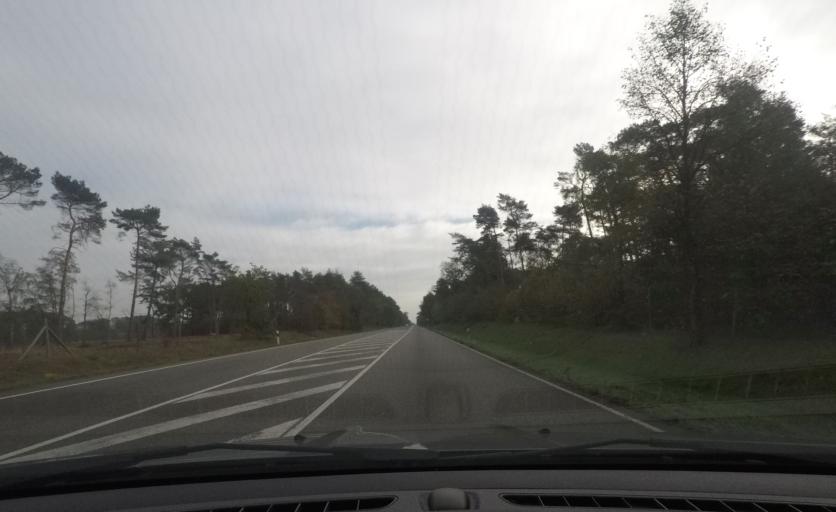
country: DE
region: North Rhine-Westphalia
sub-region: Regierungsbezirk Munster
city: Velen
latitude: 51.8558
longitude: 6.9819
